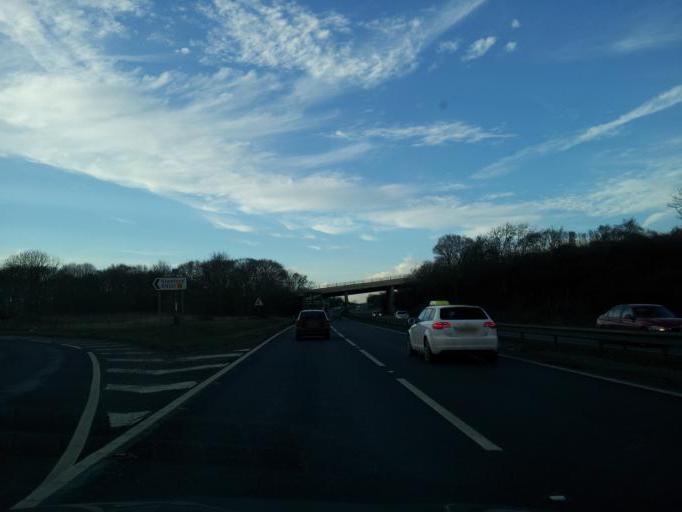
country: GB
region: England
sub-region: District of Rutland
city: Tinwell
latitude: 52.6453
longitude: -0.5039
